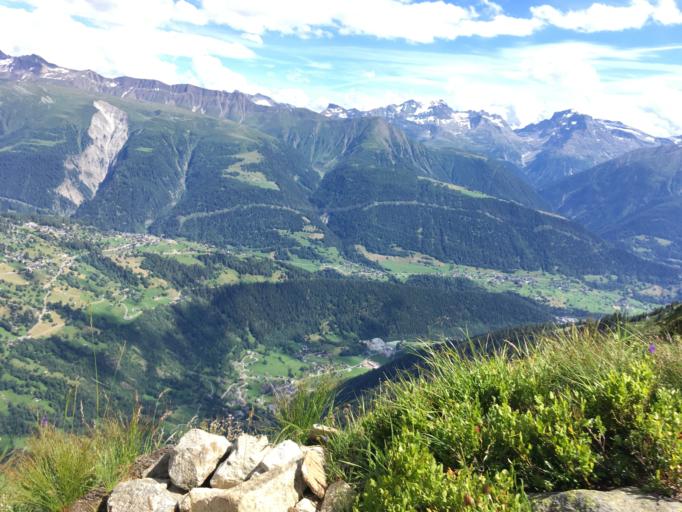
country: CH
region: Valais
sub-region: Goms District
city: Fiesch
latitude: 46.4407
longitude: 8.1196
